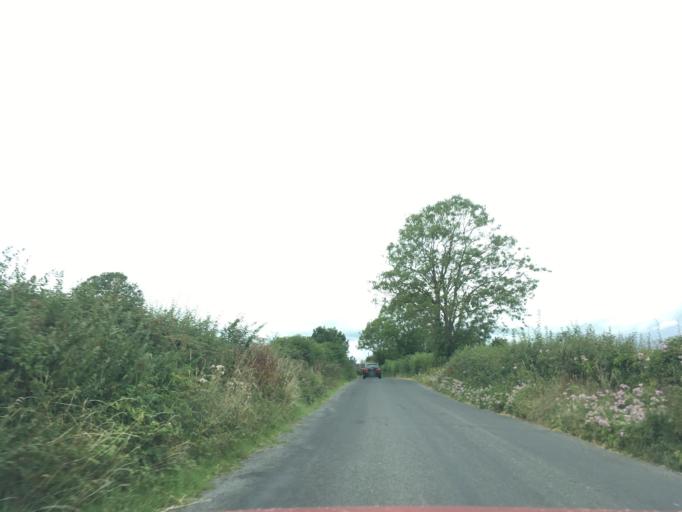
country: IE
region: Munster
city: Cahir
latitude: 52.4561
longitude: -7.9627
